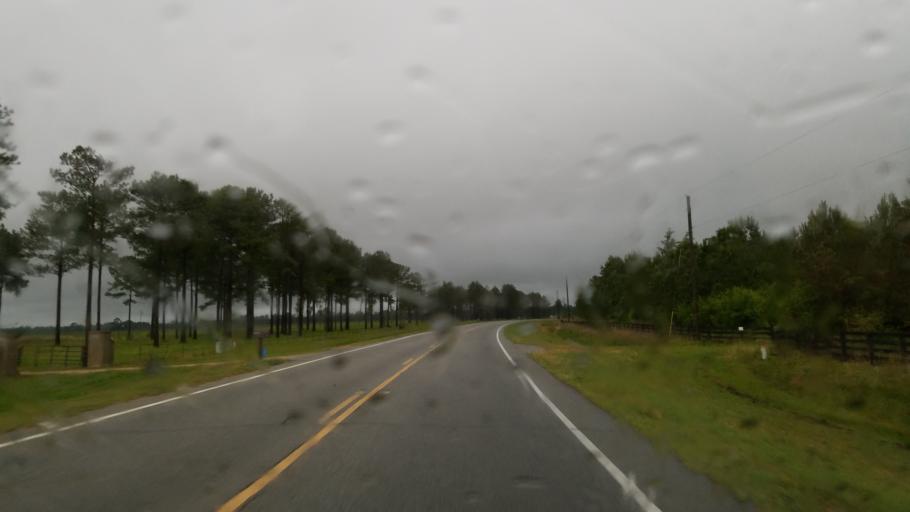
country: US
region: Georgia
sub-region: Lanier County
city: Lakeland
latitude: 31.0383
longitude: -83.0196
